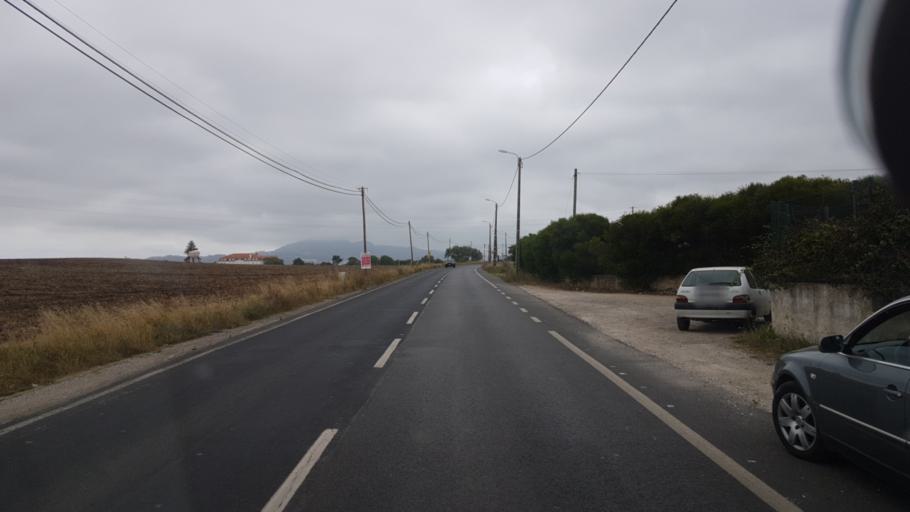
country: PT
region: Lisbon
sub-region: Sintra
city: Pero Pinheiro
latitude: 38.8440
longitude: -9.3381
